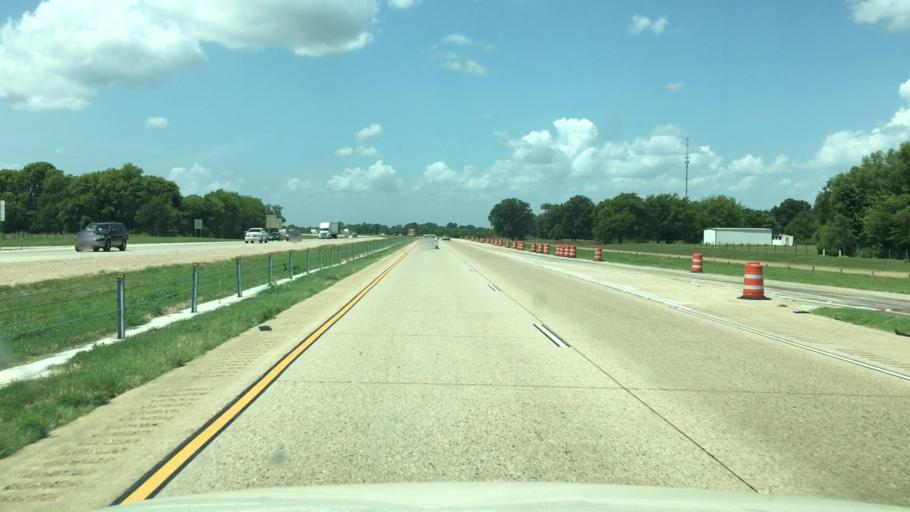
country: US
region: Arkansas
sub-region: Miller County
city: Texarkana
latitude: 33.5494
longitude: -93.8790
